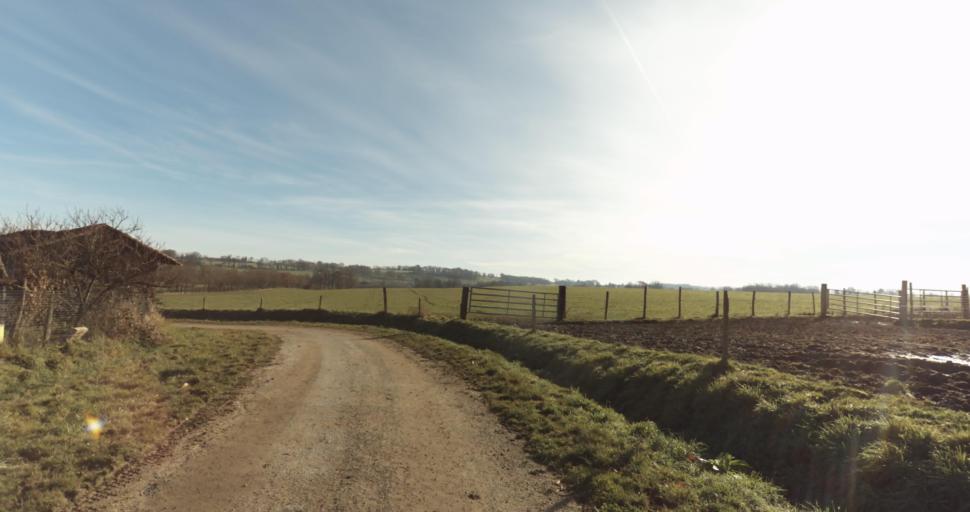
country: FR
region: Limousin
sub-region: Departement de la Haute-Vienne
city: Sereilhac
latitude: 45.7875
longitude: 1.1018
